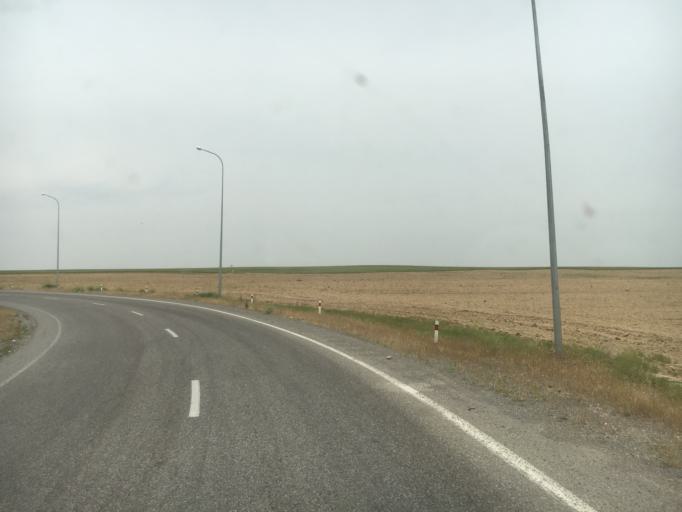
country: KZ
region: Ongtustik Qazaqstan
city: Temirlanovka
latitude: 42.5301
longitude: 69.3460
